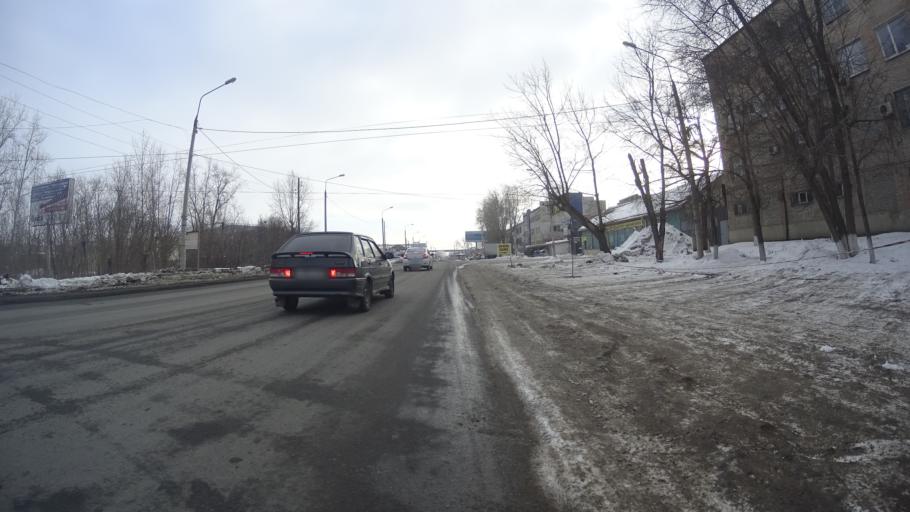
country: RU
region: Chelyabinsk
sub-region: Gorod Chelyabinsk
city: Chelyabinsk
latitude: 55.1227
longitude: 61.3859
